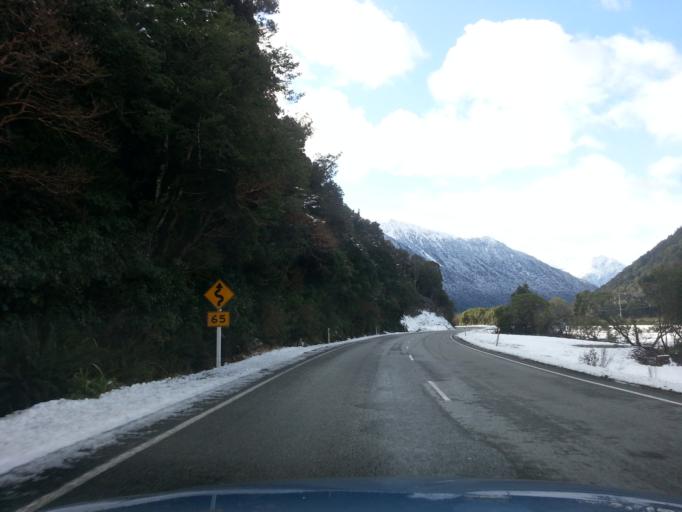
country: NZ
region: West Coast
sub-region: Grey District
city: Greymouth
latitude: -42.8242
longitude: 171.5622
